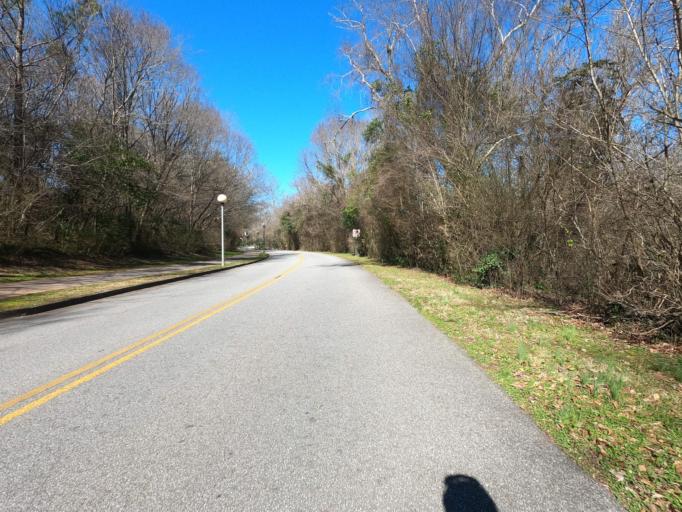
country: US
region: Georgia
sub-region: Clarke County
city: Athens
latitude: 33.9425
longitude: -83.3678
